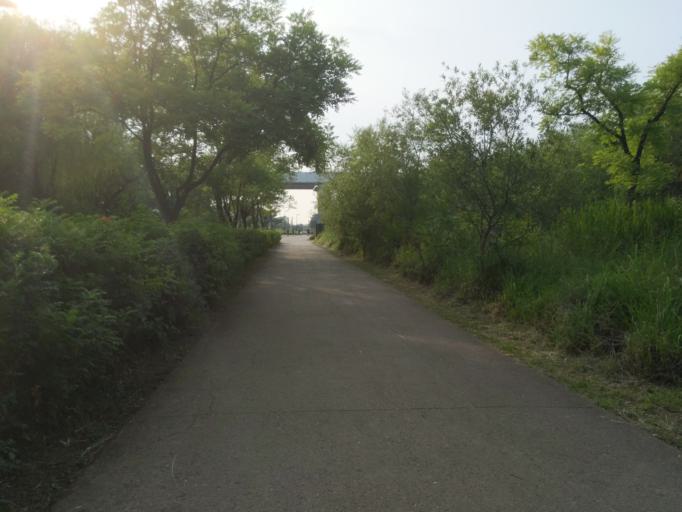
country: KR
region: Gyeonggi-do
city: Kwangmyong
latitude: 37.5362
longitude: 126.9063
